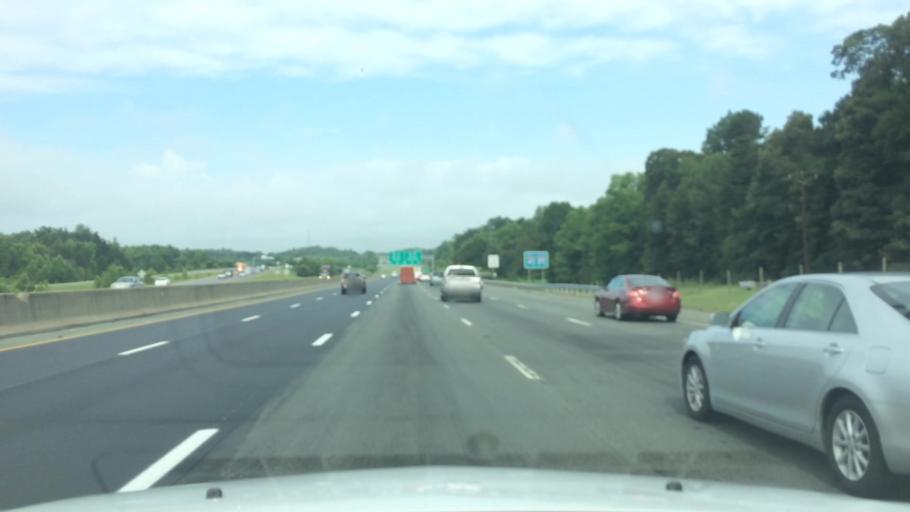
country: US
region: North Carolina
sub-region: Guilford County
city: McLeansville
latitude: 36.0595
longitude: -79.6681
